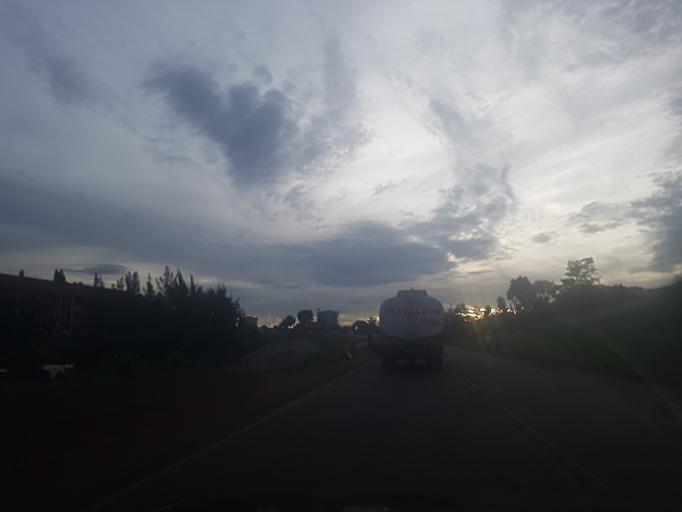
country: UG
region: Central Region
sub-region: Wakiso District
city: Kireka
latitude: 0.3658
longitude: 32.6082
